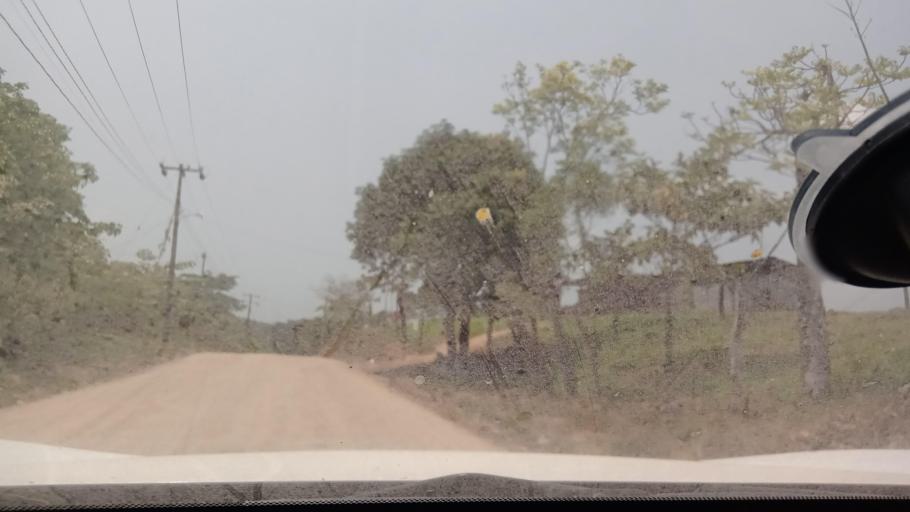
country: MX
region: Chiapas
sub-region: Tecpatan
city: Raudales Malpaso
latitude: 17.4549
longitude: -93.7944
